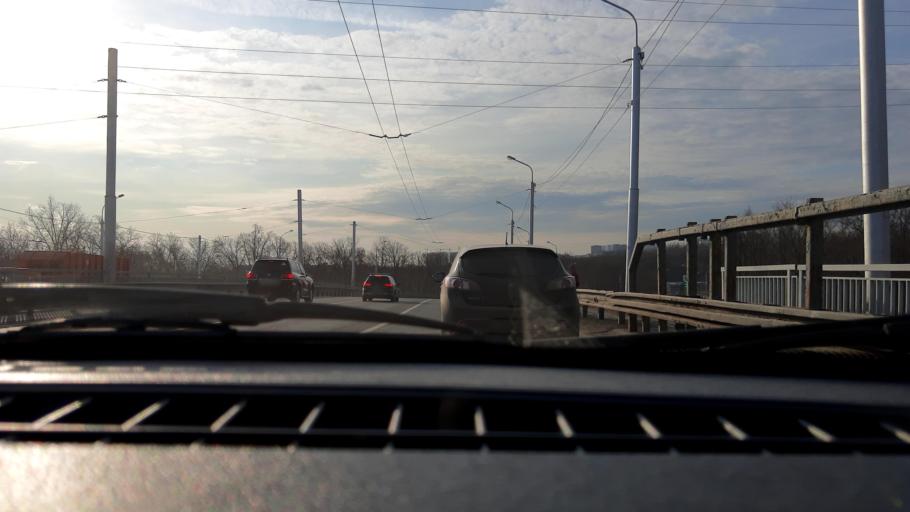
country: RU
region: Bashkortostan
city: Ufa
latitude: 54.8073
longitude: 56.0496
